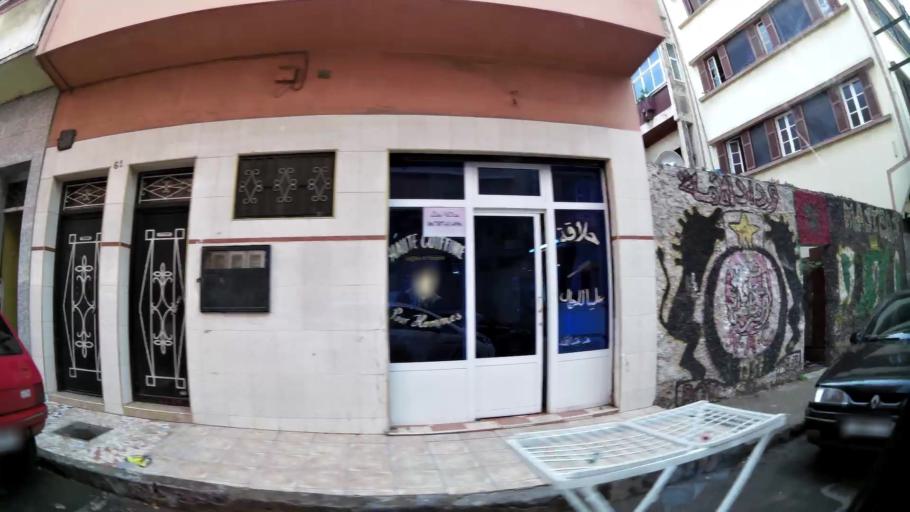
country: MA
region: Grand Casablanca
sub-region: Casablanca
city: Casablanca
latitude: 33.5693
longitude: -7.5842
